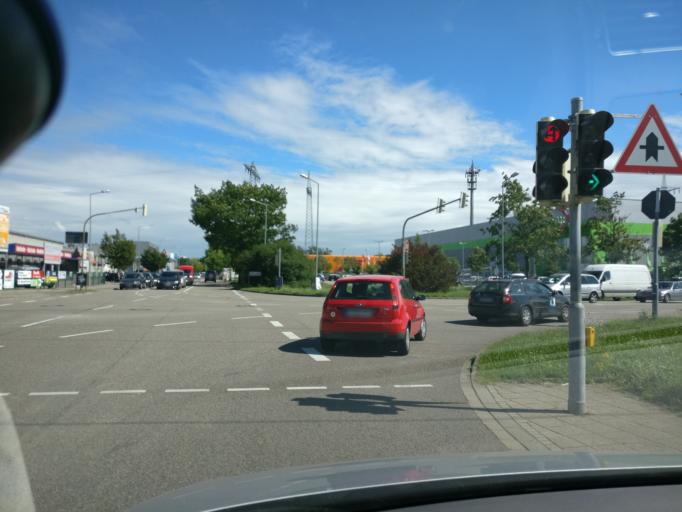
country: DE
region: Baden-Wuerttemberg
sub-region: Karlsruhe Region
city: Karlsruhe
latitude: 49.0207
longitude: 8.4575
